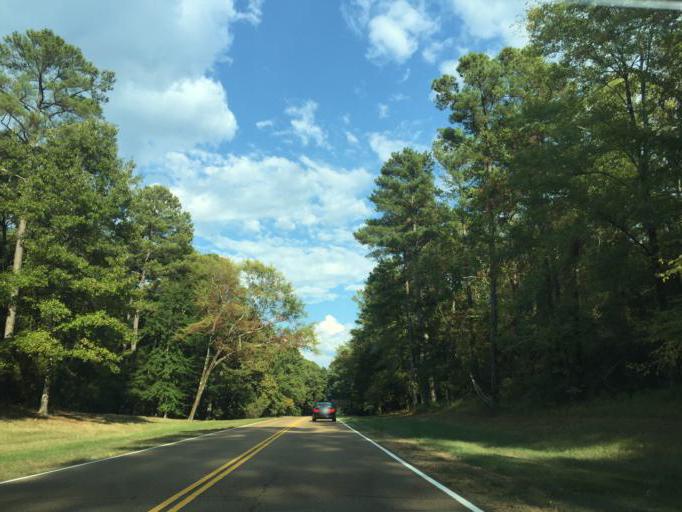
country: US
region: Mississippi
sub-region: Madison County
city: Ridgeland
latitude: 32.4270
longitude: -90.1216
